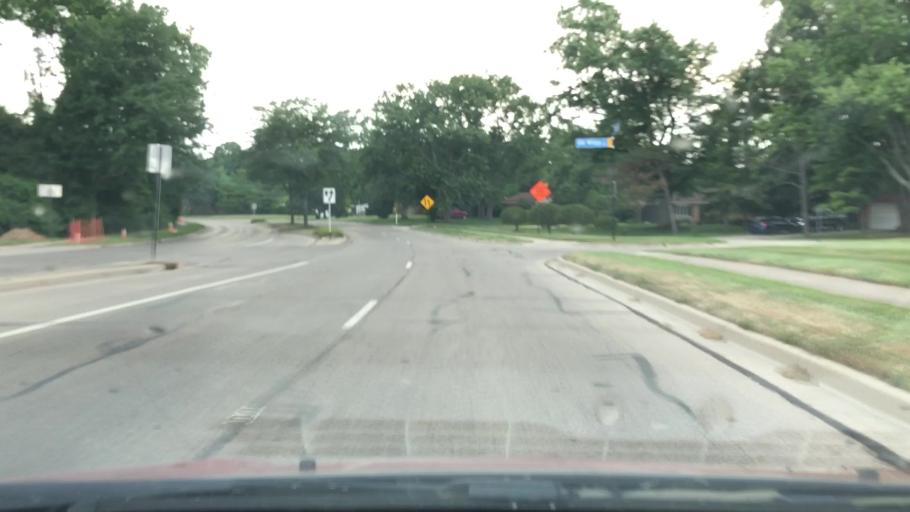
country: US
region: Ohio
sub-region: Greene County
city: Bellbrook
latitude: 39.6610
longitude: -84.1115
